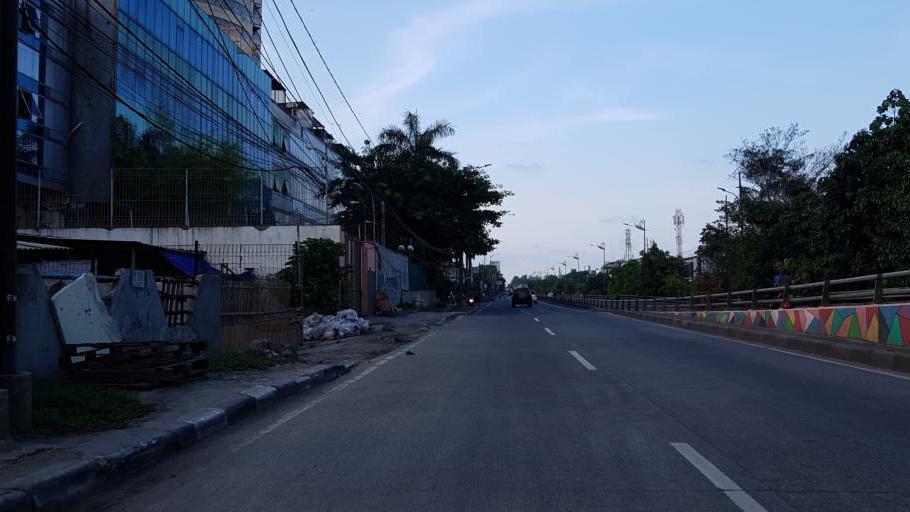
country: ID
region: Jakarta Raya
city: Jakarta
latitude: -6.1419
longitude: 106.7932
